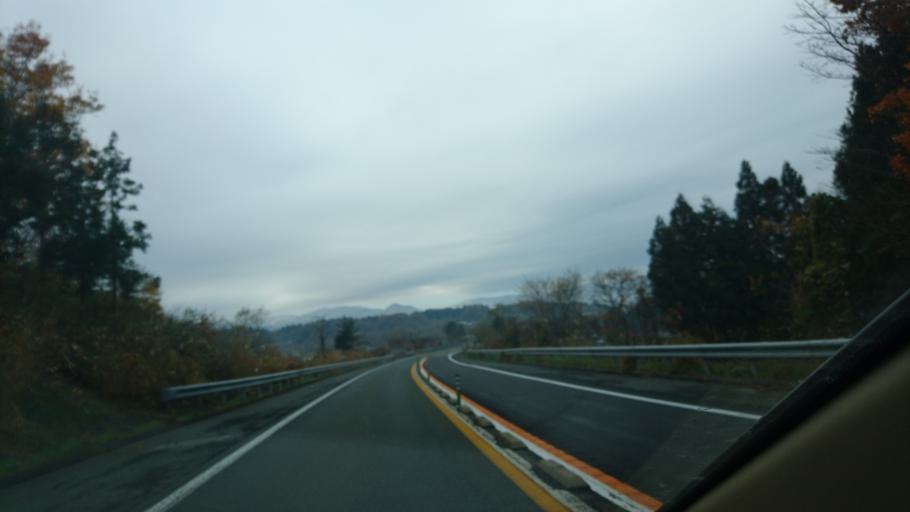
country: JP
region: Iwate
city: Kitakami
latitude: 39.2767
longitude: 141.0502
